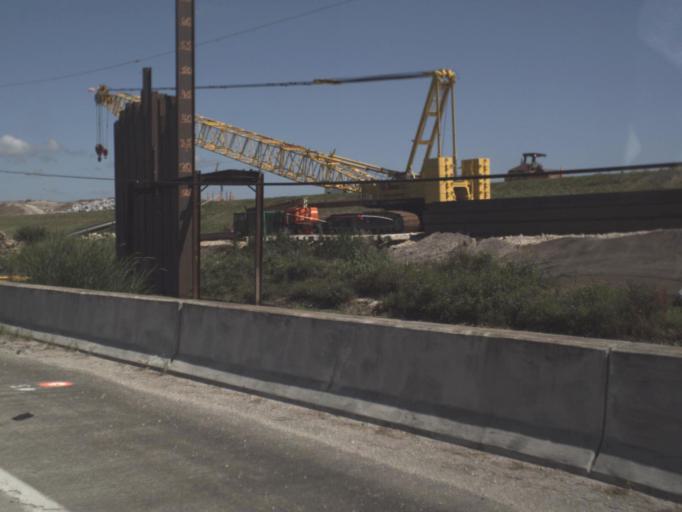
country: US
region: Florida
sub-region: Glades County
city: Moore Haven
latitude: 26.8853
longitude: -81.1225
